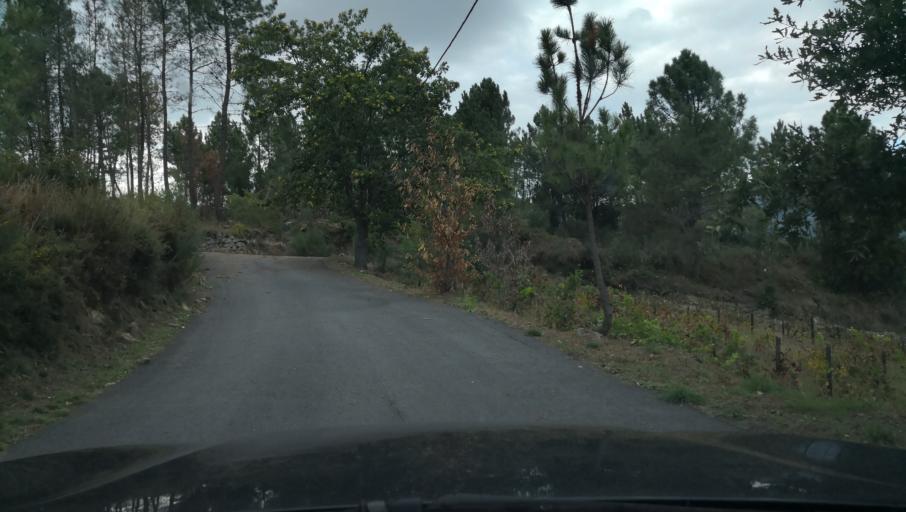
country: PT
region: Vila Real
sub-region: Vila Real
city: Vila Real
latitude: 41.2890
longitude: -7.7651
